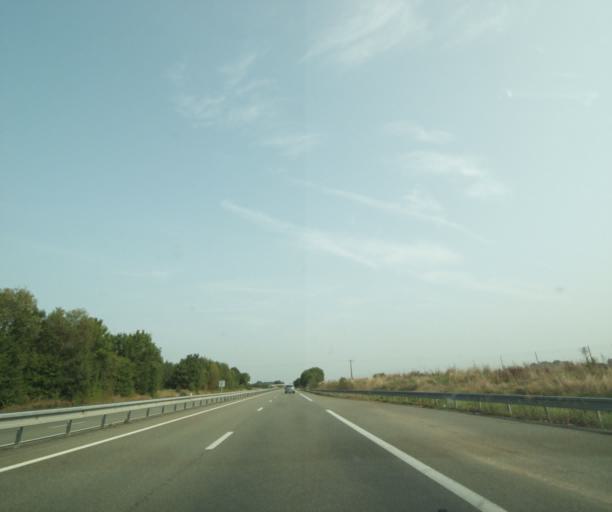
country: FR
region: Pays de la Loire
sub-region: Departement de la Sarthe
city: Sainte-Jamme-sur-Sarthe
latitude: 48.1557
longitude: 0.1429
